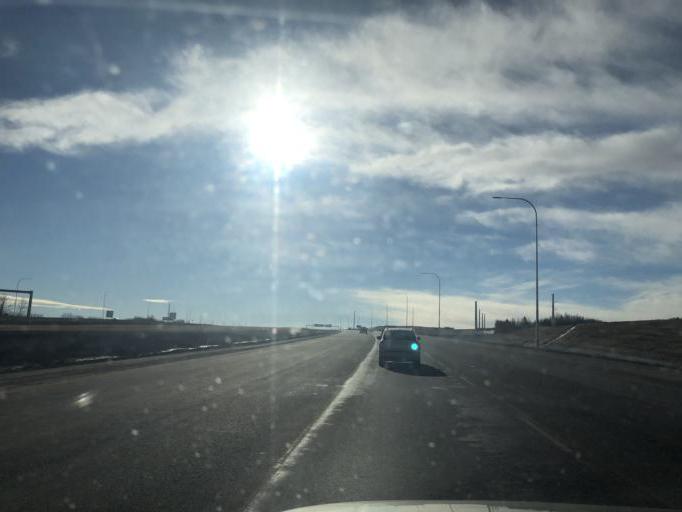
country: CA
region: Alberta
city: Calgary
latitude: 50.9867
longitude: -114.1665
